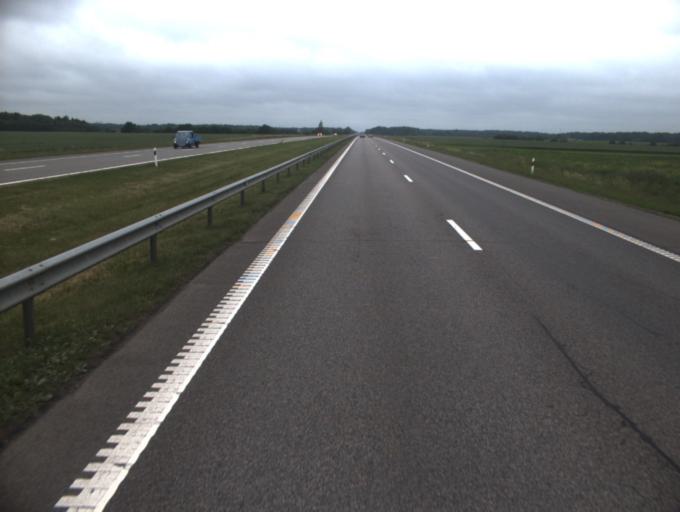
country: LT
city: Vilkija
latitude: 55.1143
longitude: 23.7675
